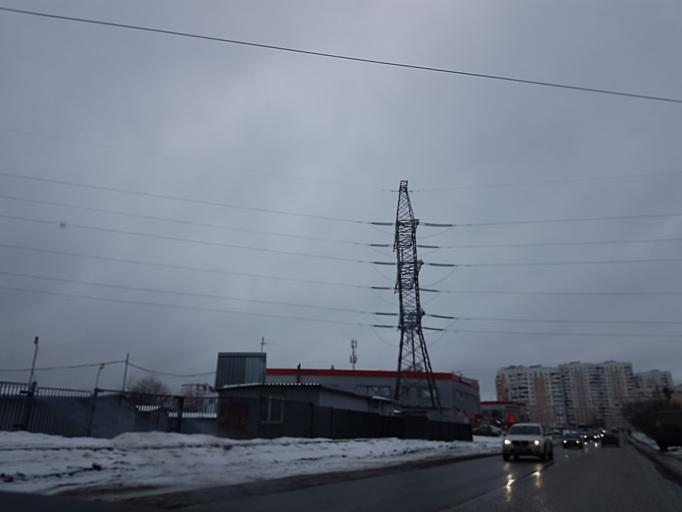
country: RU
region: Moskovskaya
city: Pavshino
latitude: 55.8251
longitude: 37.3547
